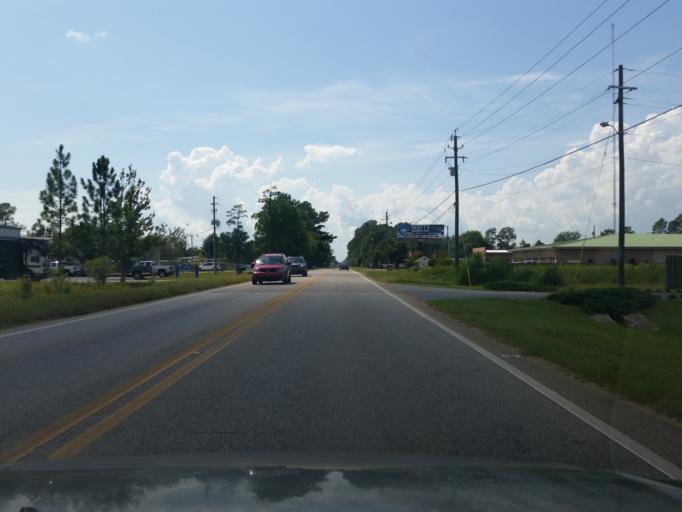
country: US
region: Alabama
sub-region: Baldwin County
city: Spanish Fort
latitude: 30.6768
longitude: -87.8317
